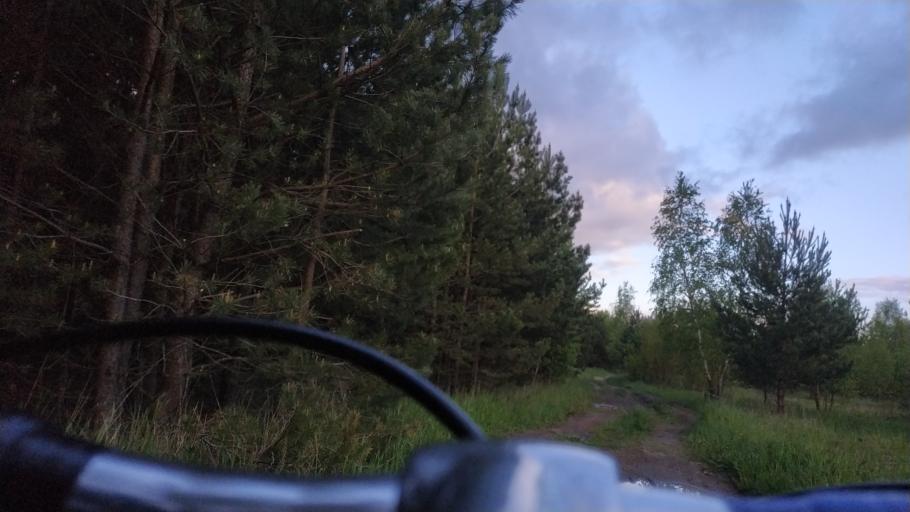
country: RU
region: Moskovskaya
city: Ramenskoye
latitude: 55.5948
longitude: 38.2881
